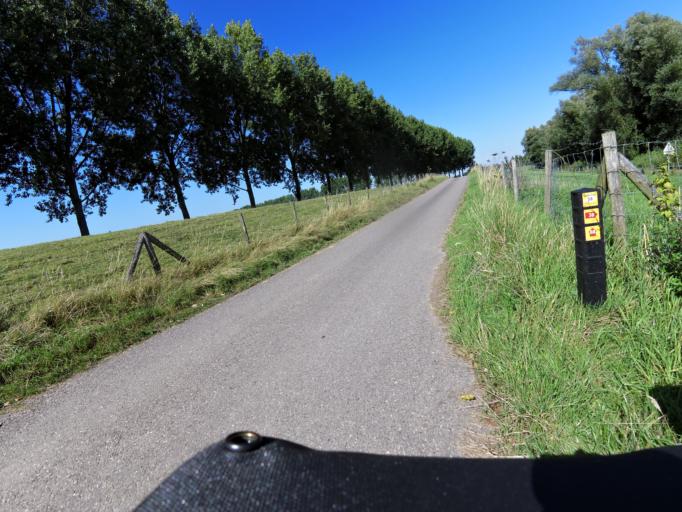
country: NL
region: South Holland
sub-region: Gemeente Dordrecht
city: Dordrecht
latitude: 51.7537
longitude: 4.7233
